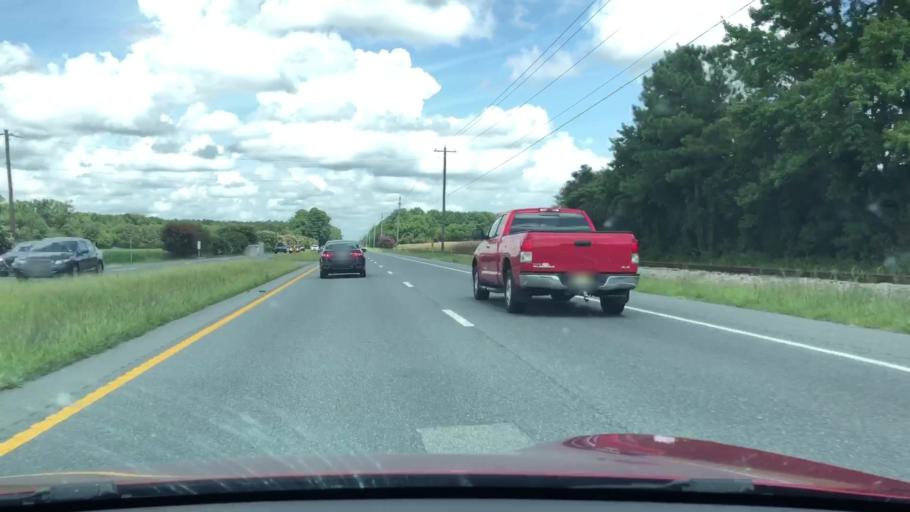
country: US
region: Virginia
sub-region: Northampton County
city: Exmore
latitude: 37.4608
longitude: -75.8679
